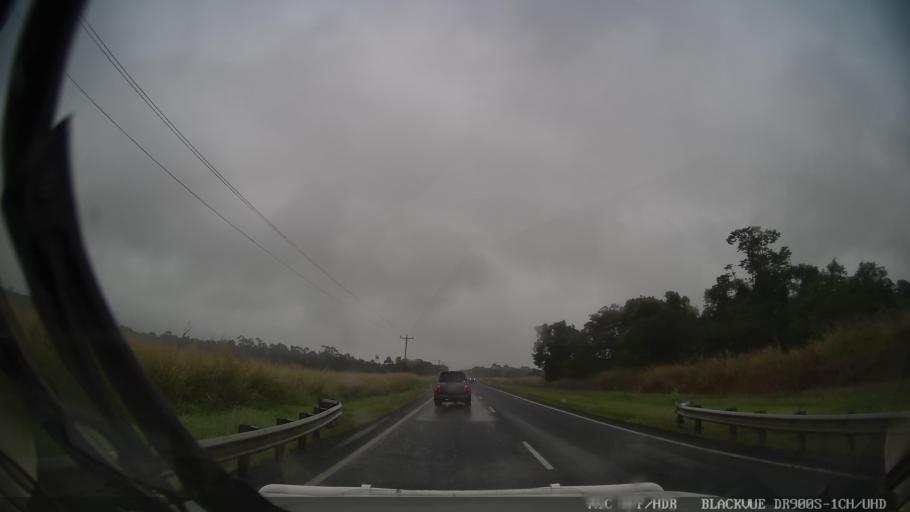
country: AU
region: Queensland
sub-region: Cassowary Coast
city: Innisfail
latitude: -17.6545
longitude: 146.0353
